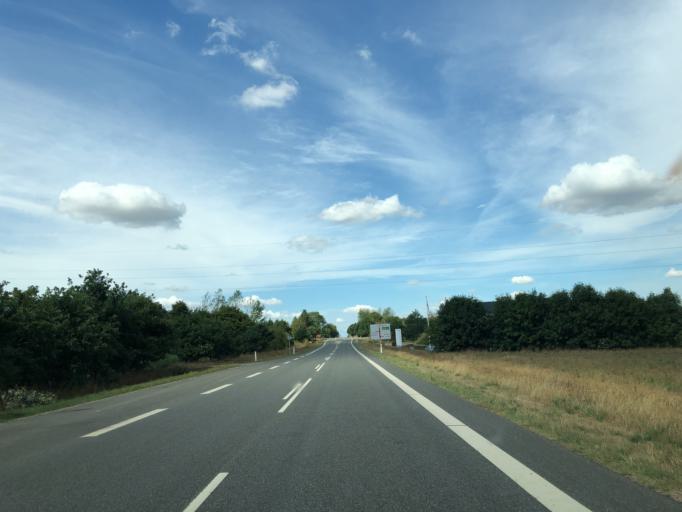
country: DK
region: Central Jutland
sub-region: Ikast-Brande Kommune
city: Bording Kirkeby
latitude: 56.1396
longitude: 9.2956
